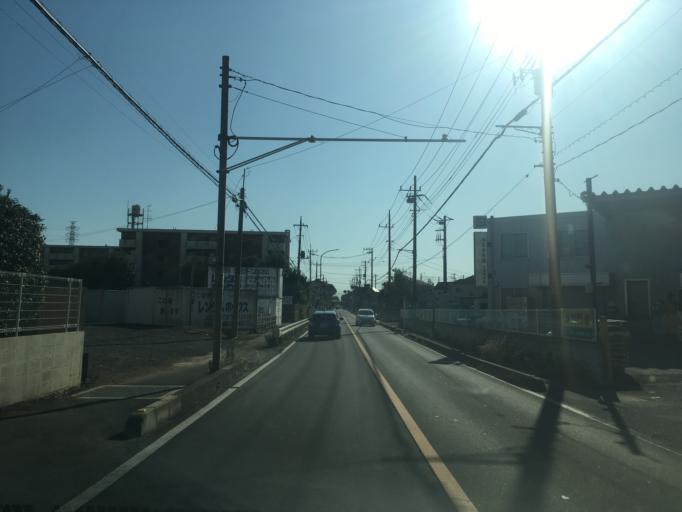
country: JP
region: Saitama
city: Kawagoe
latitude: 35.8776
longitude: 139.4747
